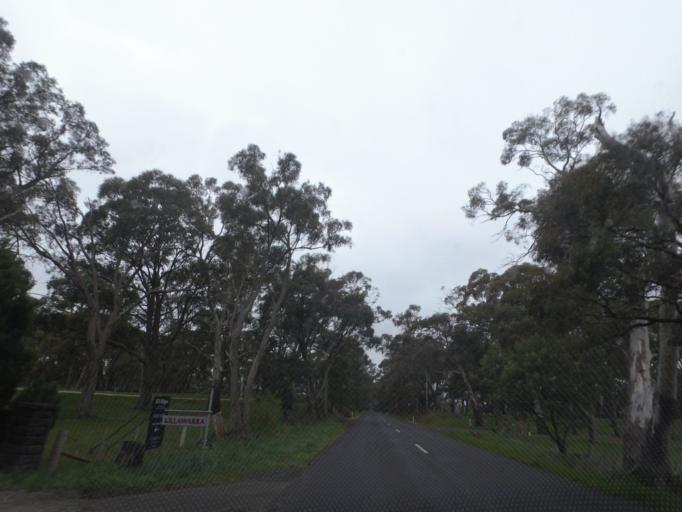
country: AU
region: Victoria
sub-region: Hume
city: Sunbury
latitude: -37.3438
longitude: 144.5891
